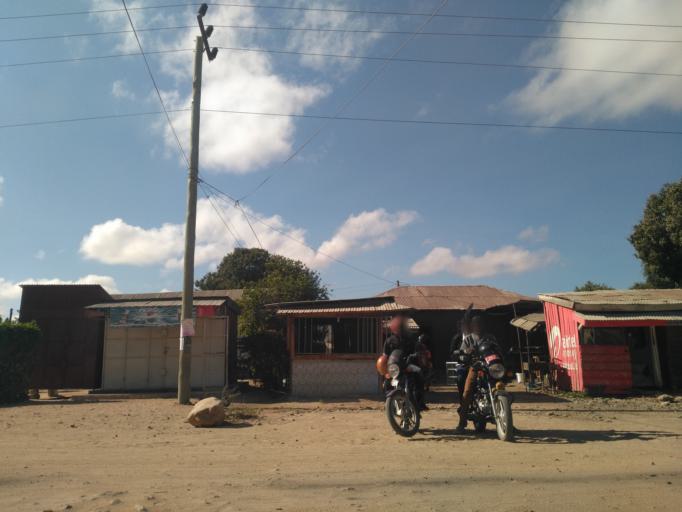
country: TZ
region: Dodoma
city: Dodoma
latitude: -6.1862
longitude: 35.7371
